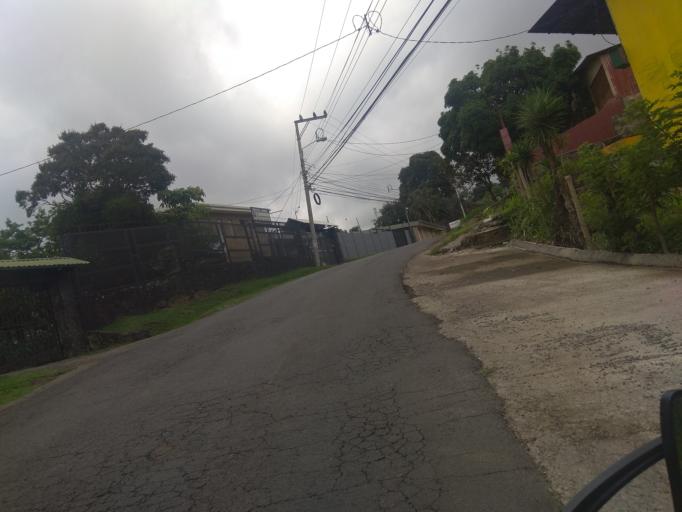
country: CR
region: Heredia
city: San Josecito
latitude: 10.0270
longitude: -84.1076
